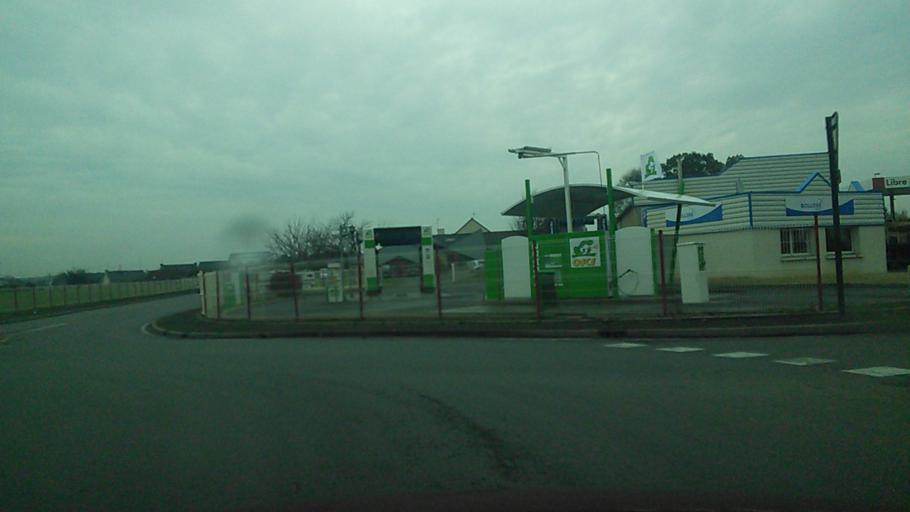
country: FR
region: Brittany
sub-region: Departement des Cotes-d'Armor
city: Pommeret
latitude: 48.4823
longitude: -2.6461
